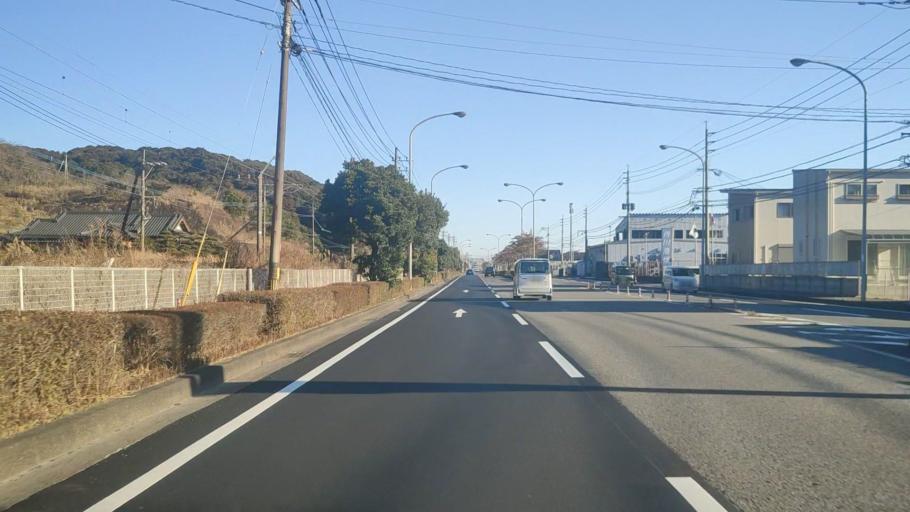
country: JP
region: Miyazaki
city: Nobeoka
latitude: 32.4515
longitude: 131.6406
